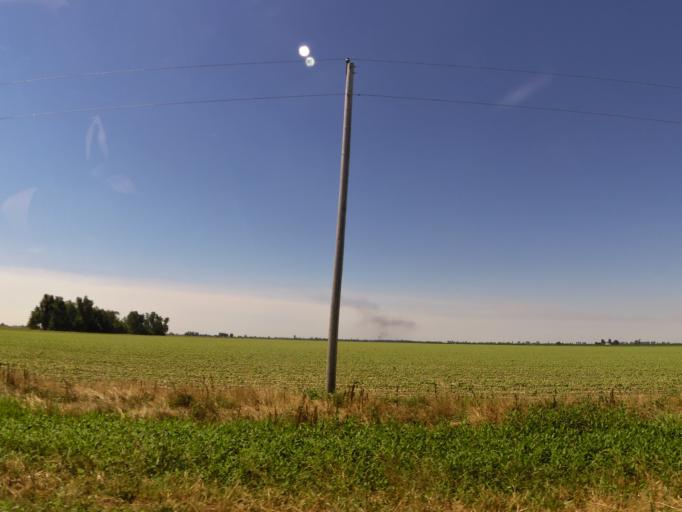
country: US
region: Missouri
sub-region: New Madrid County
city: Lilbourn
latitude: 36.5539
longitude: -89.7258
